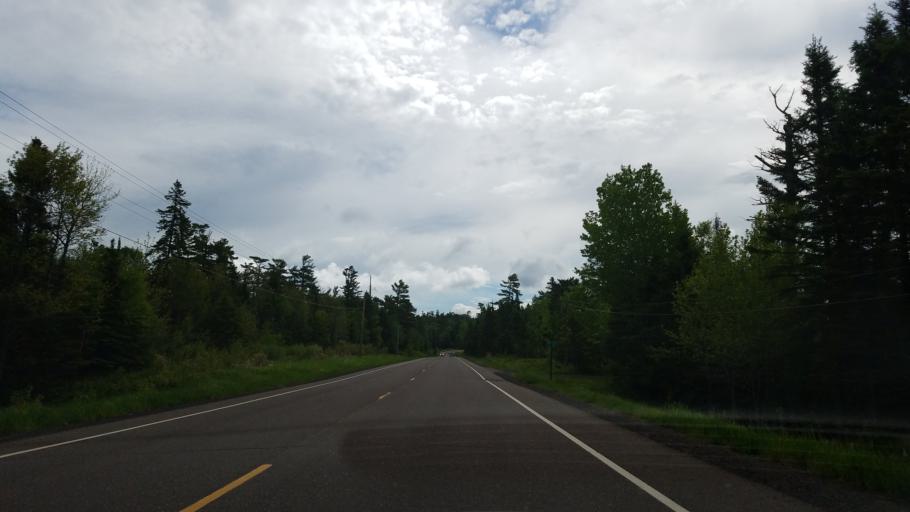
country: US
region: Minnesota
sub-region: Lake County
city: Two Harbors
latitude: 47.0950
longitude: -91.5705
